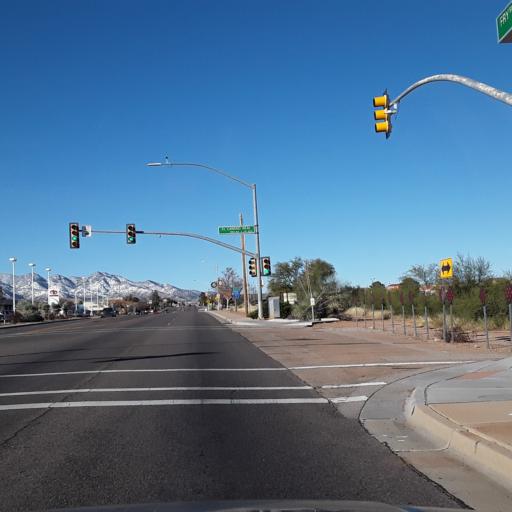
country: US
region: Arizona
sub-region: Cochise County
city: Sierra Vista
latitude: 31.5547
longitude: -110.2719
